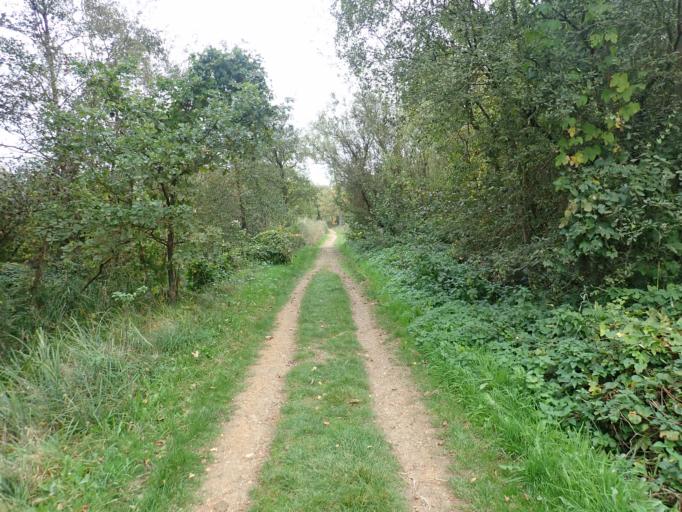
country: BE
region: Flanders
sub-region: Provincie Antwerpen
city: Rumst
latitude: 51.0569
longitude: 4.3977
